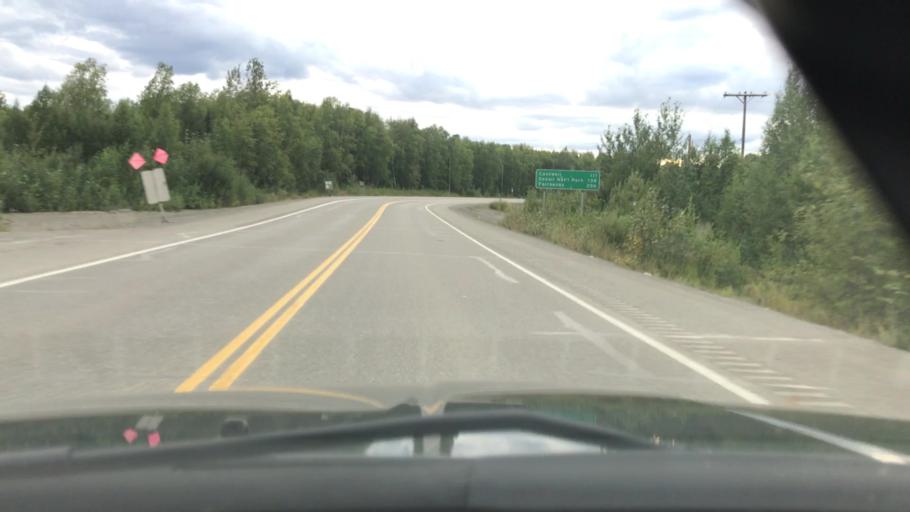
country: US
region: Alaska
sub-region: Matanuska-Susitna Borough
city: Y
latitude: 62.1387
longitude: -150.0522
